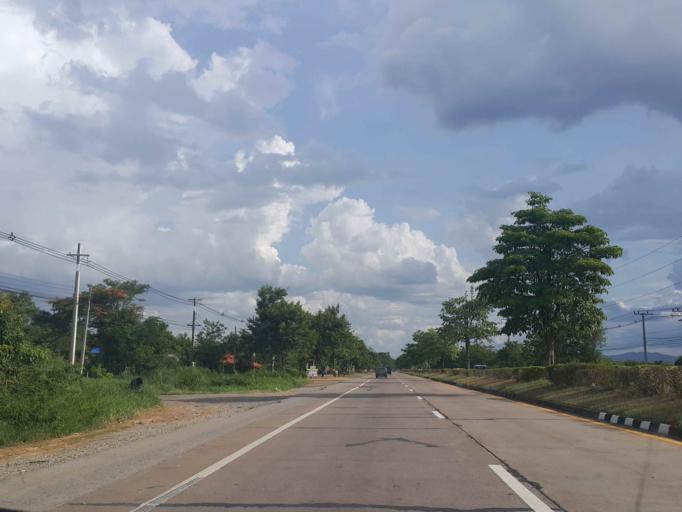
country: TH
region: Phrae
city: Sung Men
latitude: 18.0204
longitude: 100.1094
